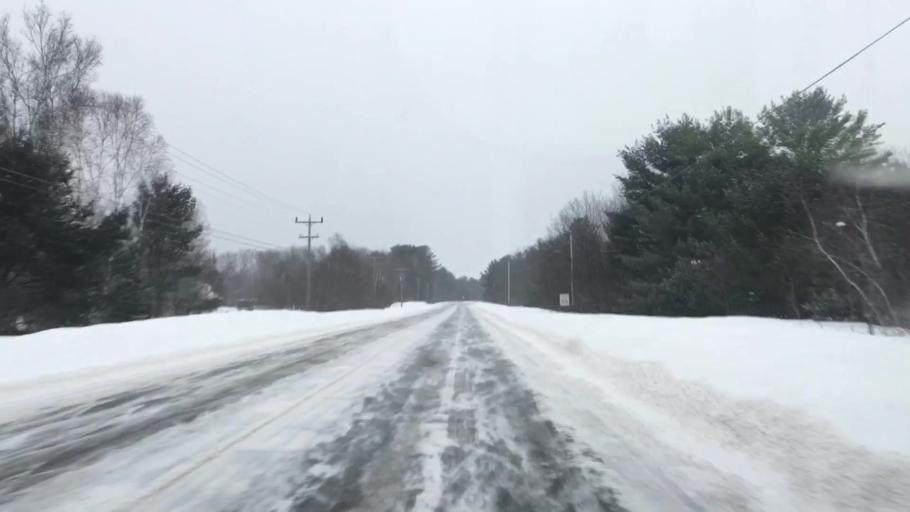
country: US
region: Maine
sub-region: Penobscot County
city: Medway
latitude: 45.5622
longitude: -68.3938
